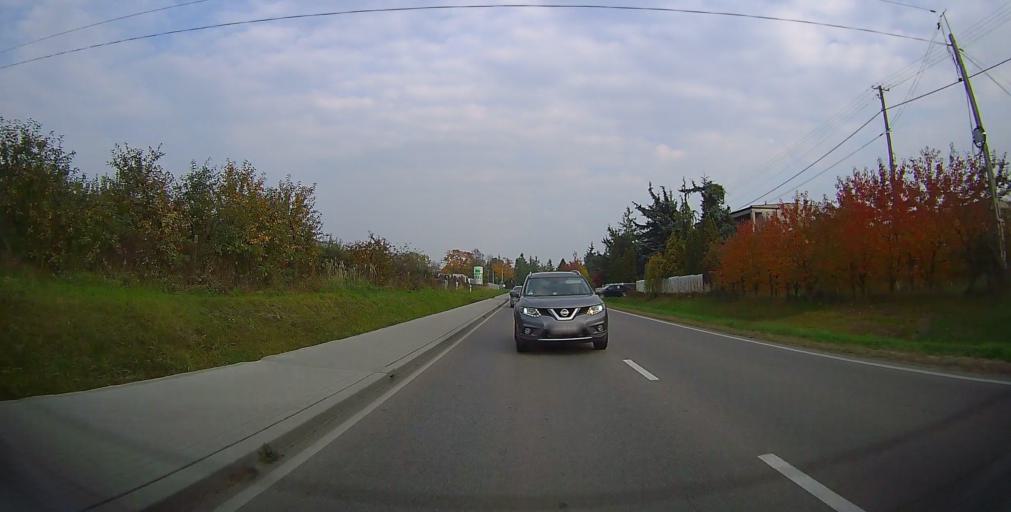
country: PL
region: Masovian Voivodeship
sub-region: Powiat grojecki
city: Belsk Duzy
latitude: 51.7742
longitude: 20.7699
